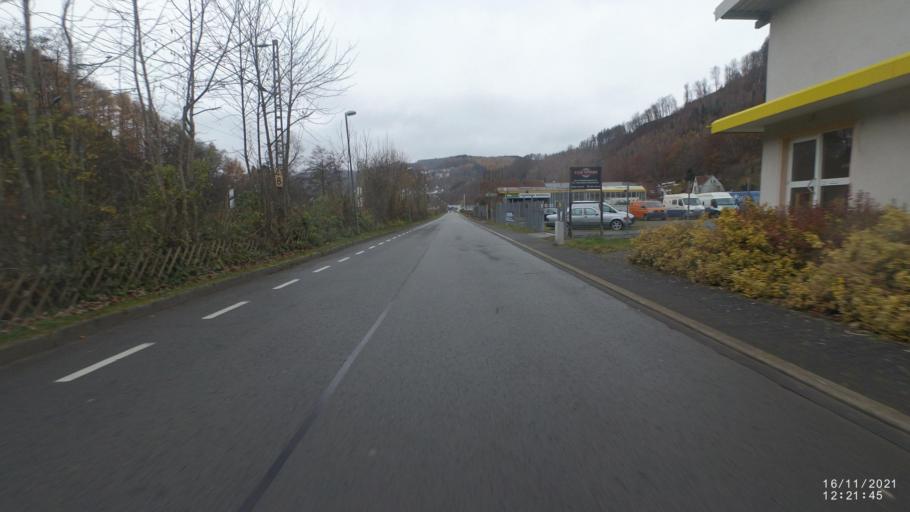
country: DE
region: North Rhine-Westphalia
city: Neuenrade
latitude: 51.2596
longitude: 7.7909
